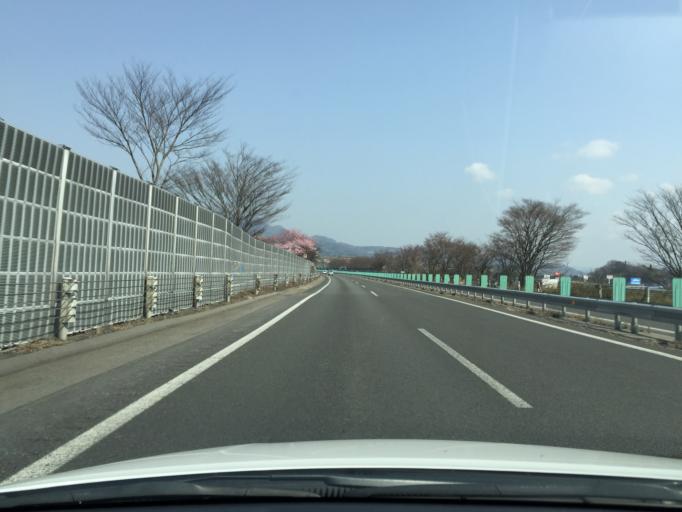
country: JP
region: Miyagi
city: Shiroishi
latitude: 37.9966
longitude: 140.6082
